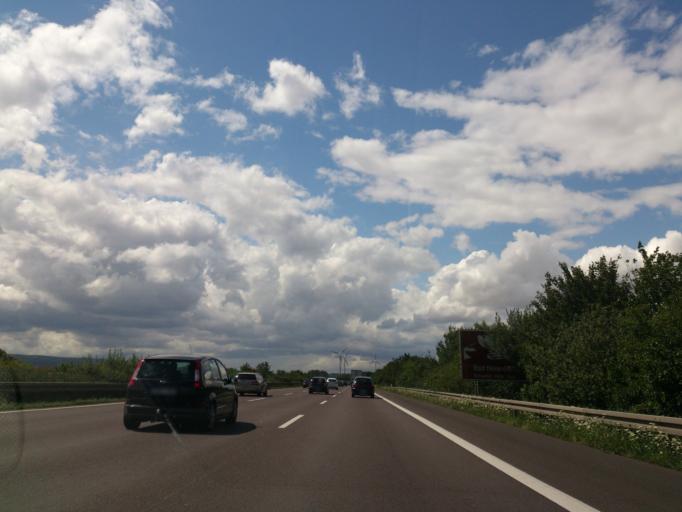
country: DE
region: Lower Saxony
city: Gross Munzel
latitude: 52.3746
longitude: 9.4546
